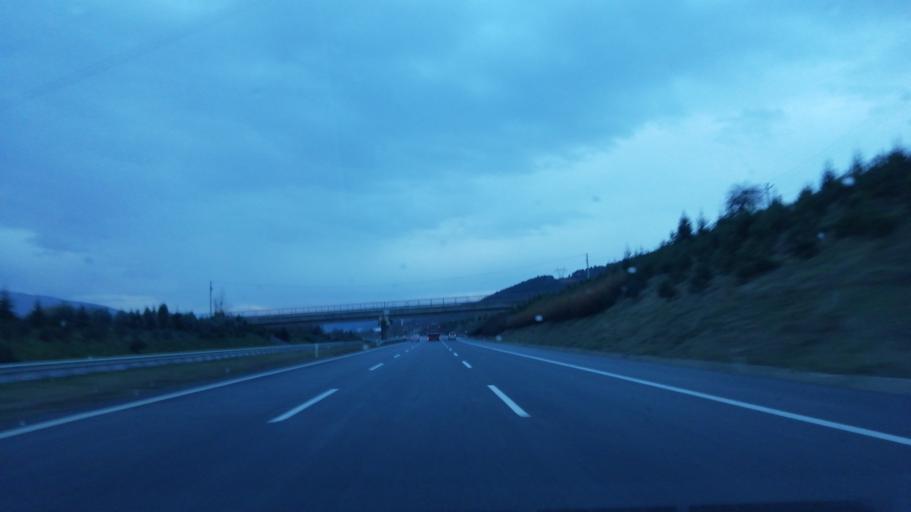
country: TR
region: Duzce
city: Kaynasli
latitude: 40.7801
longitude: 31.3445
